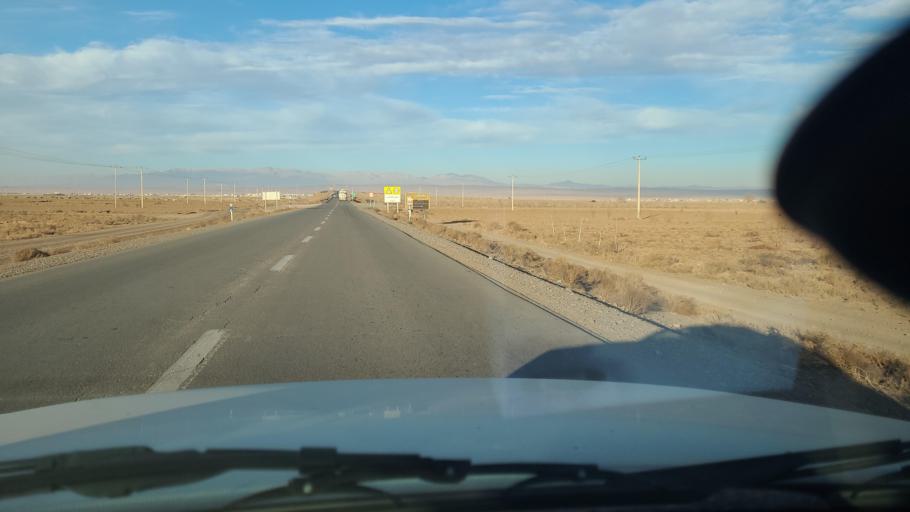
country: IR
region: Razavi Khorasan
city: Neqab
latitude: 36.5980
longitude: 57.5881
